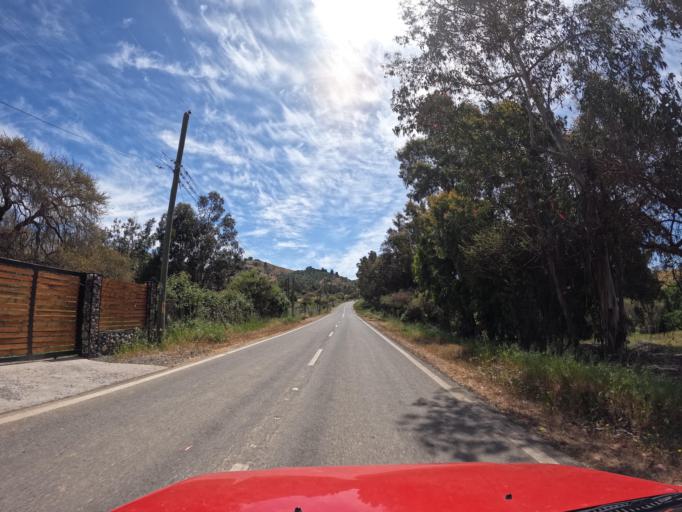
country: CL
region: Maule
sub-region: Provincia de Talca
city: Talca
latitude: -35.0540
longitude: -71.7470
